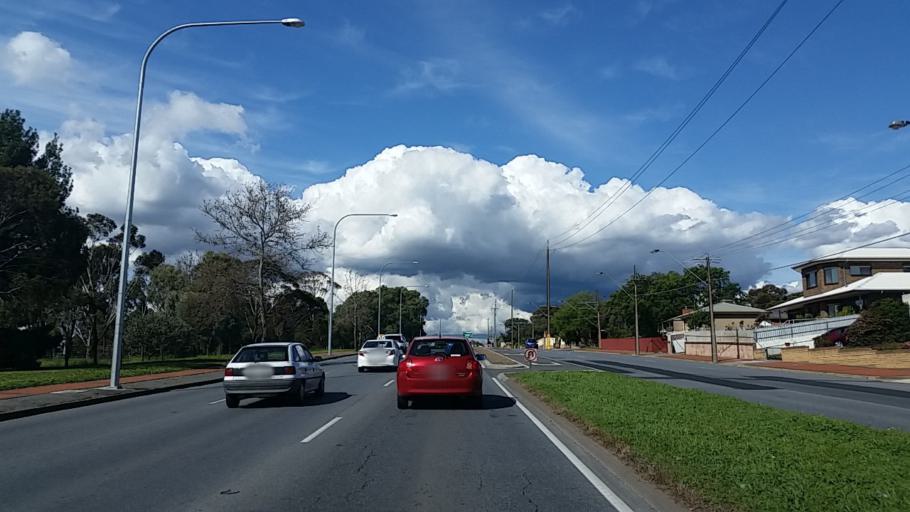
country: AU
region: South Australia
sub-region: Port Adelaide Enfield
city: Enfield
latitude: -34.8474
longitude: 138.6123
